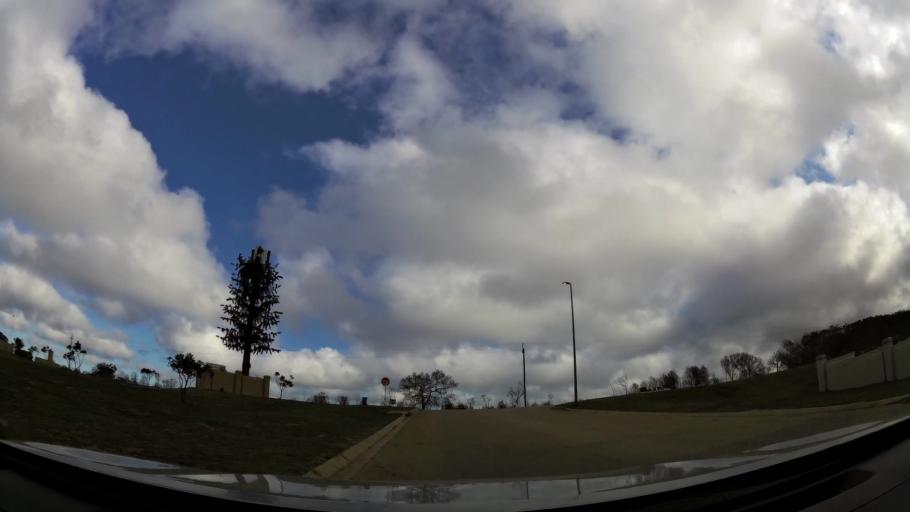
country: ZA
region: Western Cape
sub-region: Eden District Municipality
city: Plettenberg Bay
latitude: -34.0896
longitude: 23.3557
